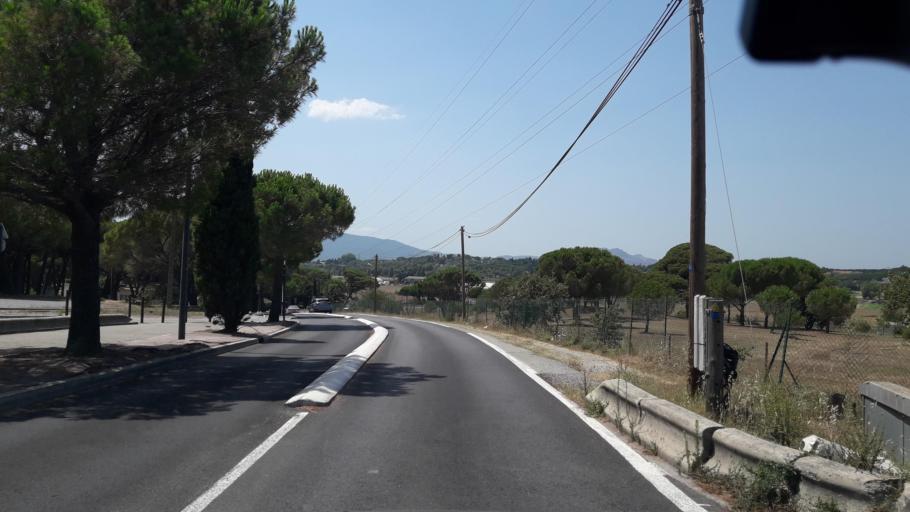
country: FR
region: Provence-Alpes-Cote d'Azur
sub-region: Departement du Var
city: Frejus
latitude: 43.4506
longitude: 6.7449
